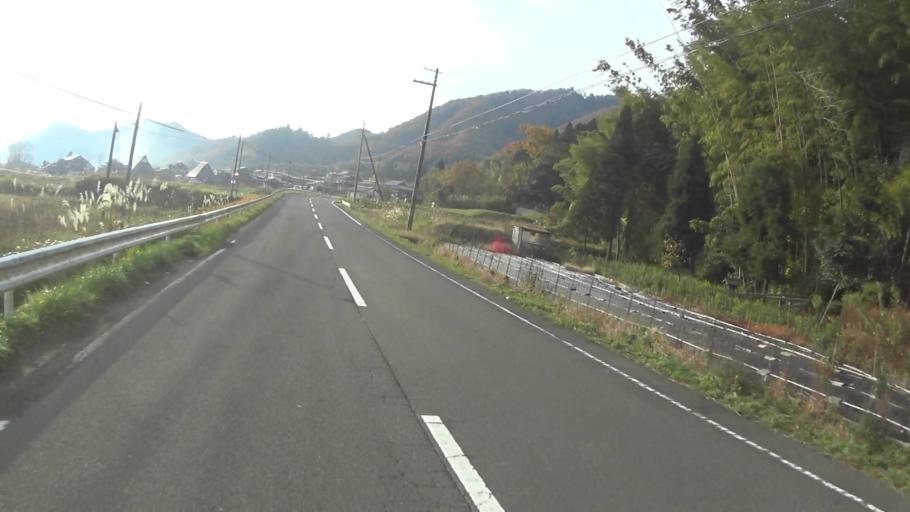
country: JP
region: Kyoto
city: Maizuru
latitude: 35.5256
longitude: 135.4149
